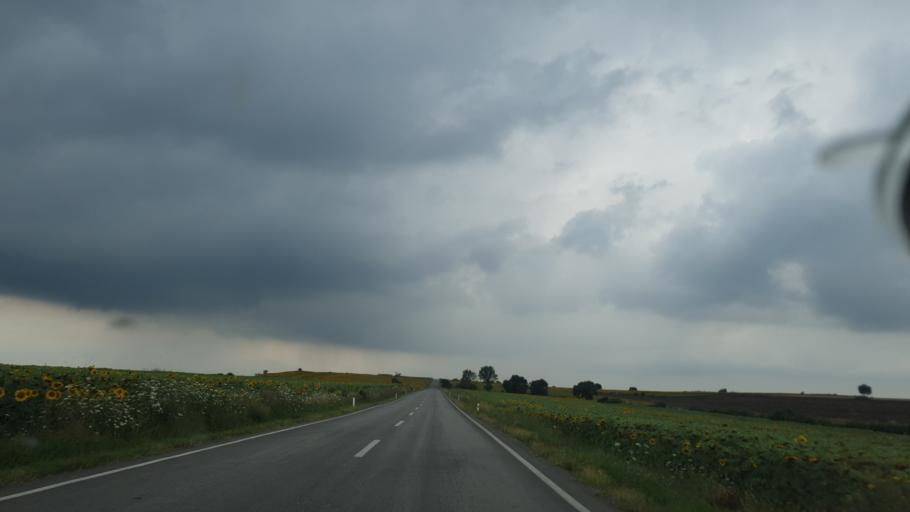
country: TR
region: Tekirdag
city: Hayrabolu
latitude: 41.2180
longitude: 26.9709
